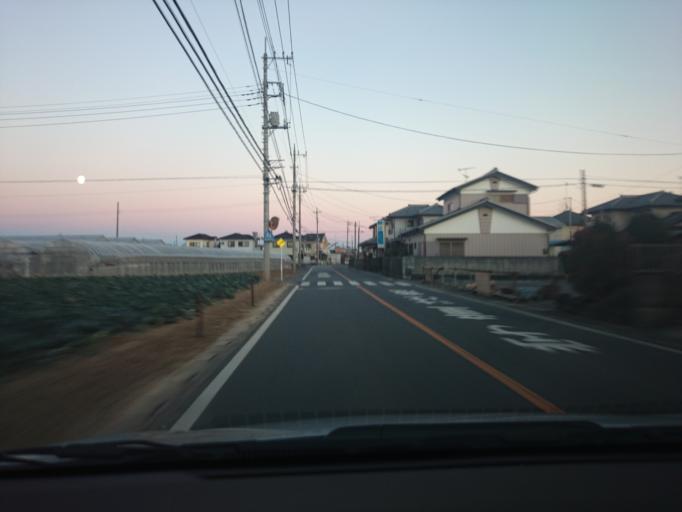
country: JP
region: Saitama
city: Fukayacho
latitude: 36.2286
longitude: 139.2665
